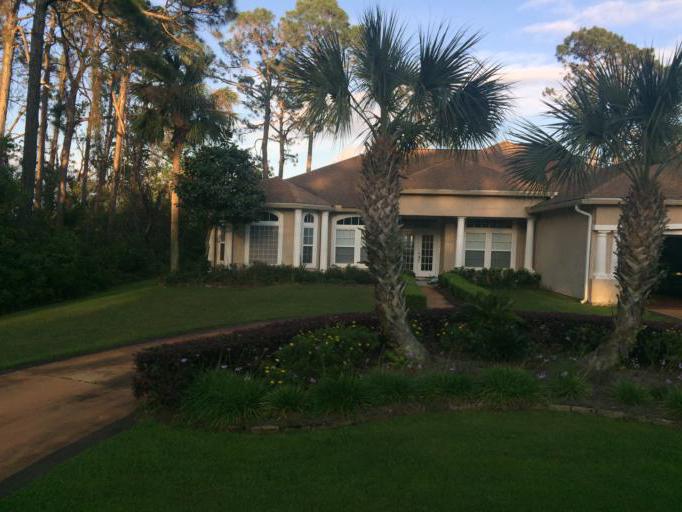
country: US
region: Florida
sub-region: Bay County
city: Panama City Beach
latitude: 30.2164
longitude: -85.8446
